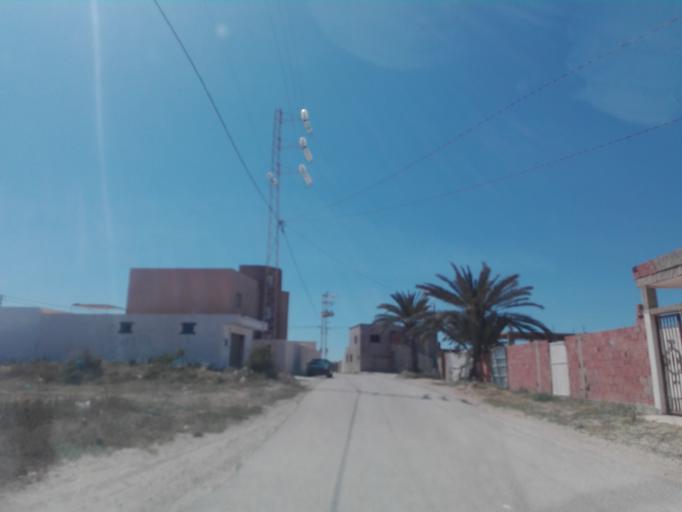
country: TN
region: Safaqis
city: Jabinyanah
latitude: 34.7404
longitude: 11.2988
